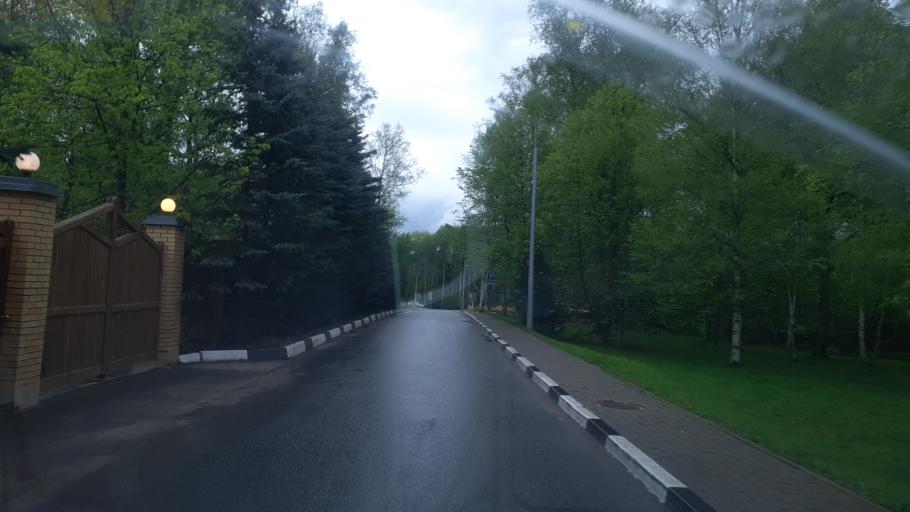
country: RU
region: Moskovskaya
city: Gorki Vtoryye
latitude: 55.7097
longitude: 37.2050
